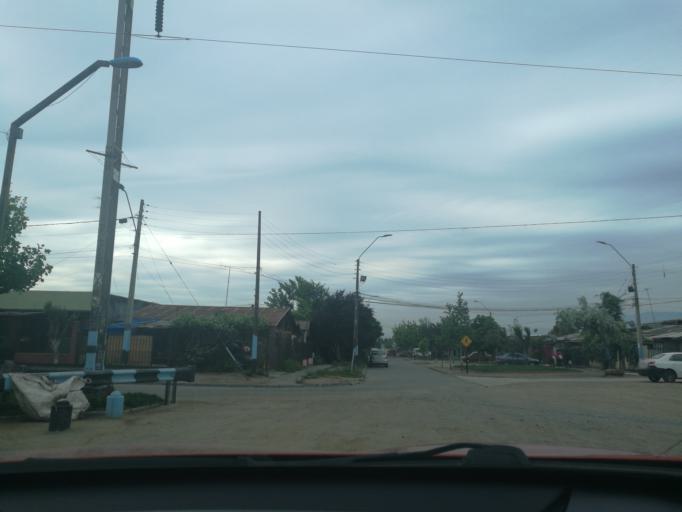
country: CL
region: O'Higgins
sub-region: Provincia de Cachapoal
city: Rancagua
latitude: -34.1664
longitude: -70.7247
